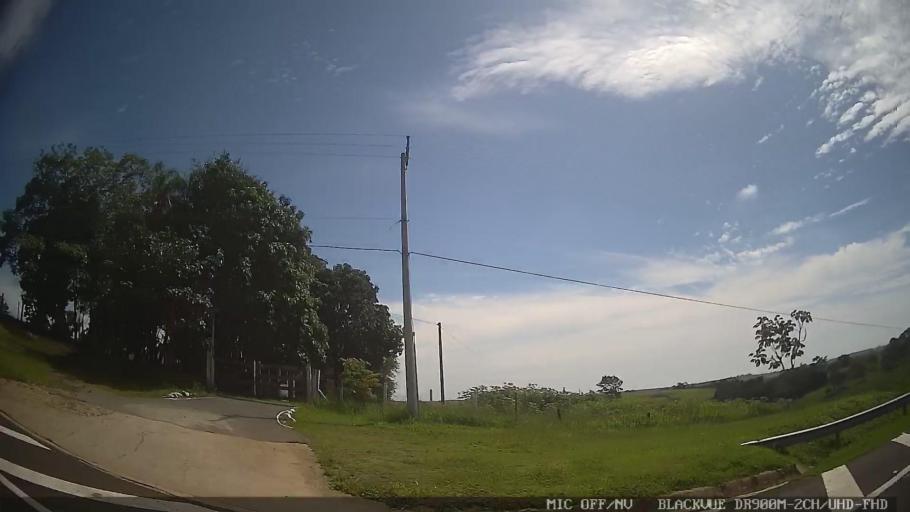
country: BR
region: Sao Paulo
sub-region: Porto Feliz
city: Porto Feliz
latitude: -23.2074
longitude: -47.5971
